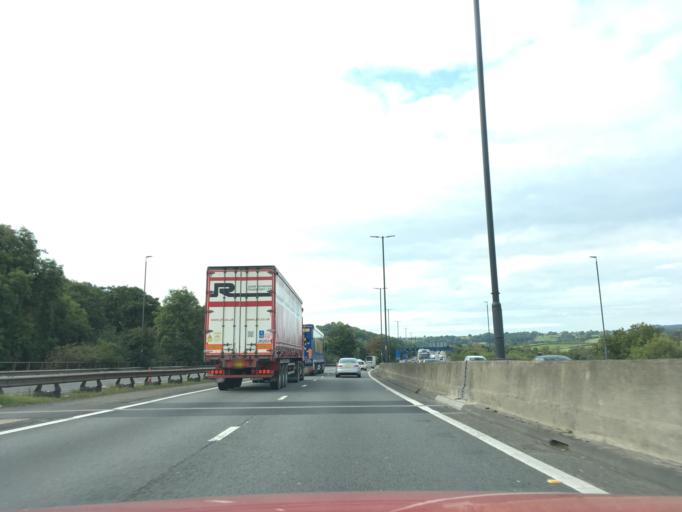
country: GB
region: Wales
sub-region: Newport
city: Newport
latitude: 51.5999
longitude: -3.0069
